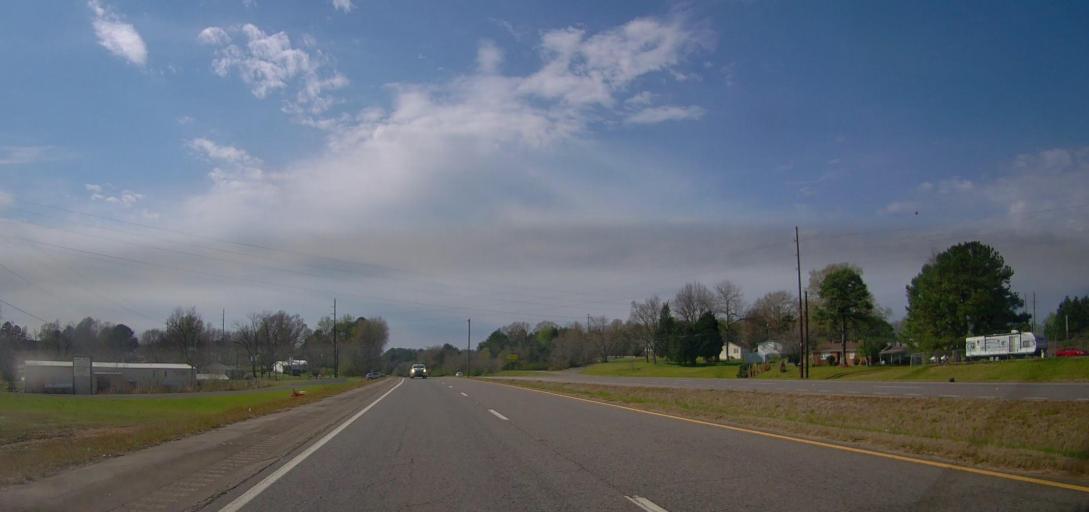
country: US
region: Alabama
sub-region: Jefferson County
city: Adamsville
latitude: 33.5982
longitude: -86.9448
